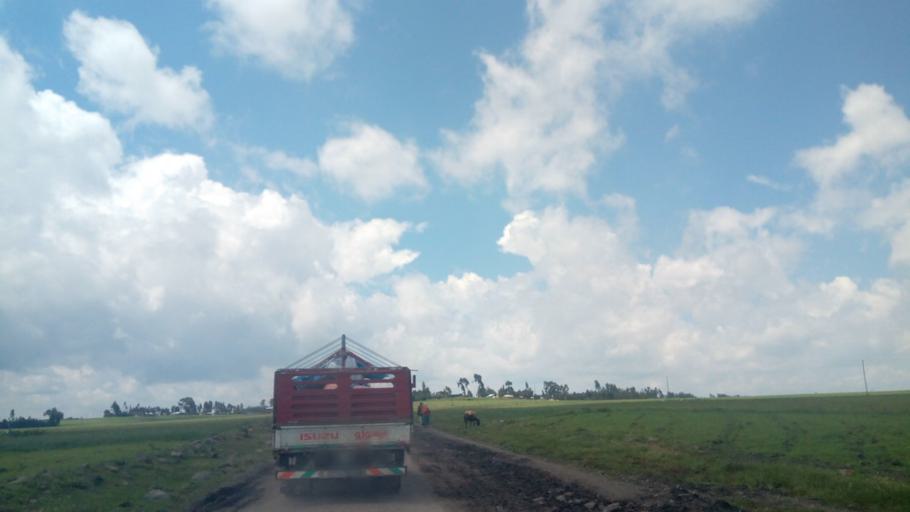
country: ET
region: Oromiya
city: Sendafa
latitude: 8.9922
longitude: 39.1246
